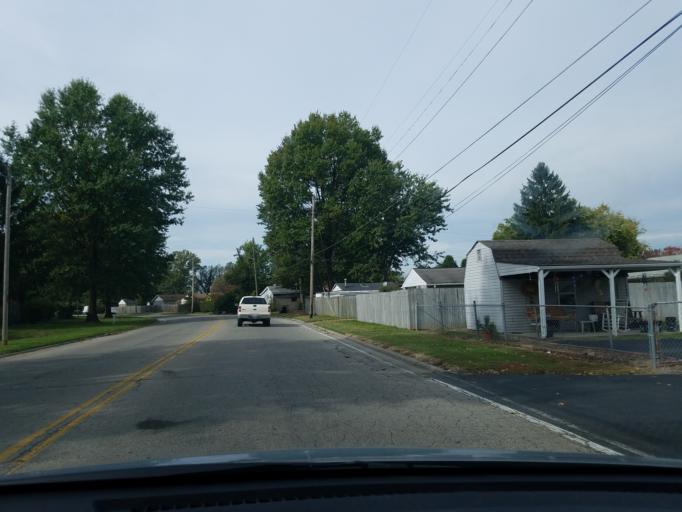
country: US
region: Indiana
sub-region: Clark County
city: Clarksville
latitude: 38.3054
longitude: -85.7567
